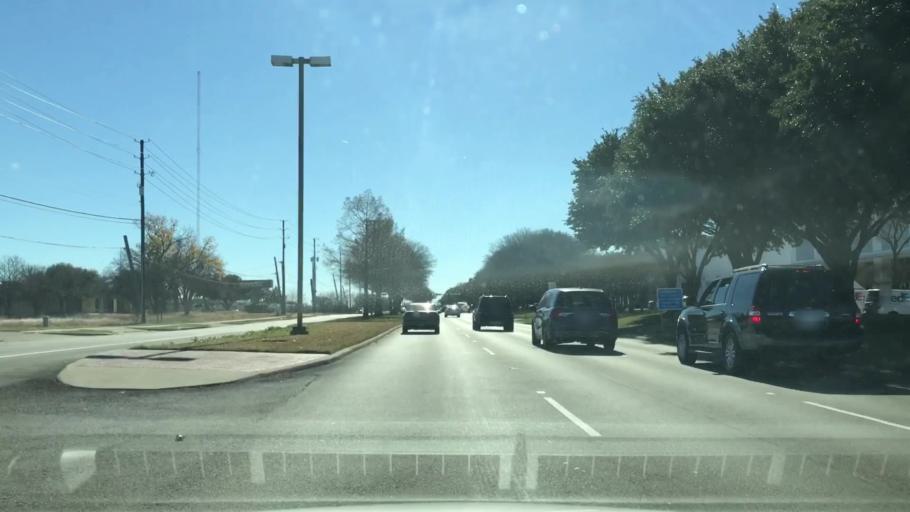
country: US
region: Texas
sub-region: Dallas County
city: Coppell
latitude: 32.9463
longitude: -96.9936
